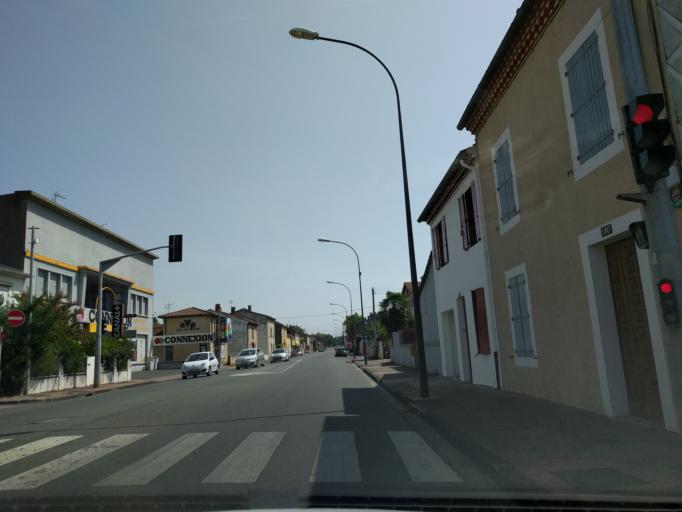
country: FR
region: Midi-Pyrenees
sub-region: Departement du Tarn
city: Castres
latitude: 43.5986
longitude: 2.2579
